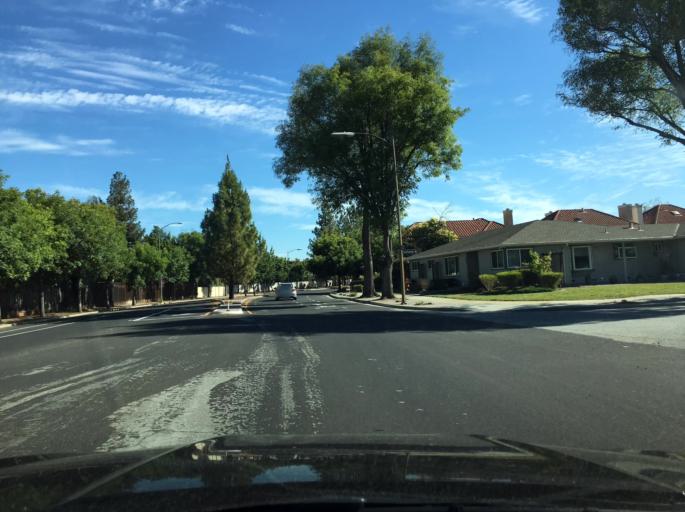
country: US
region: California
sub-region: Santa Clara County
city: Cambrian Park
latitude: 37.2340
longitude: -121.8758
